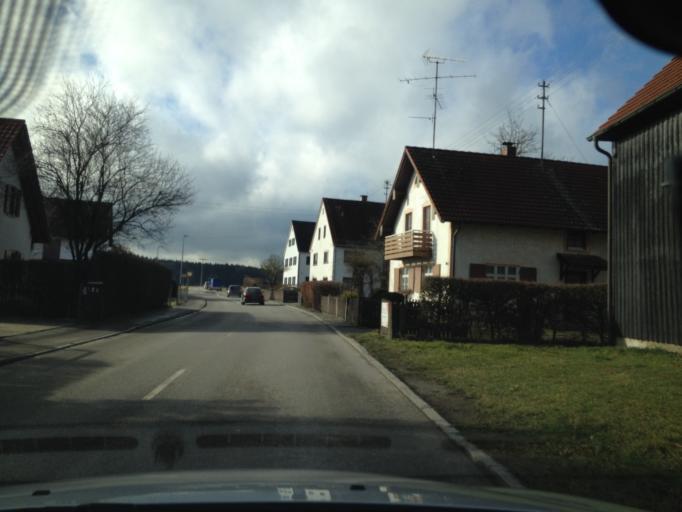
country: DE
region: Bavaria
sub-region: Swabia
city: Grossaitingen
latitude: 48.2565
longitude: 10.7282
